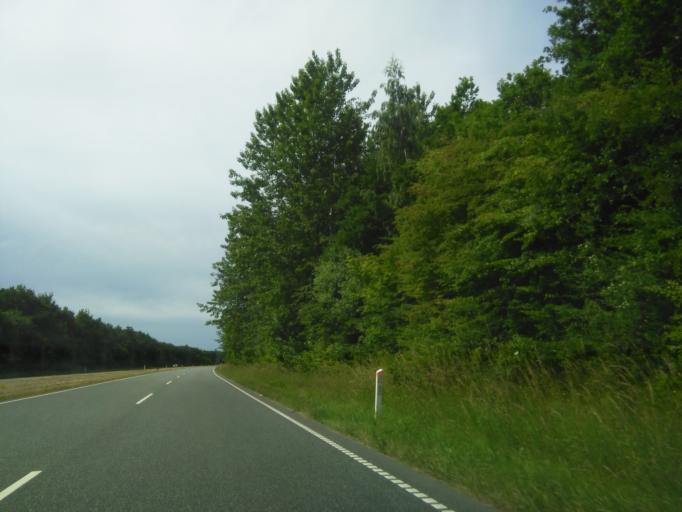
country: DK
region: Central Jutland
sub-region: Arhus Kommune
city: Tranbjerg
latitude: 56.0896
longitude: 10.1302
